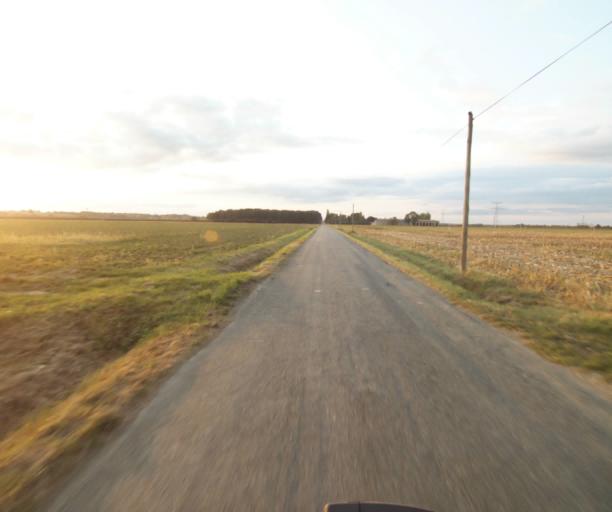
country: FR
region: Midi-Pyrenees
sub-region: Departement du Tarn-et-Garonne
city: Verdun-sur-Garonne
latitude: 43.8258
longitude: 1.2353
